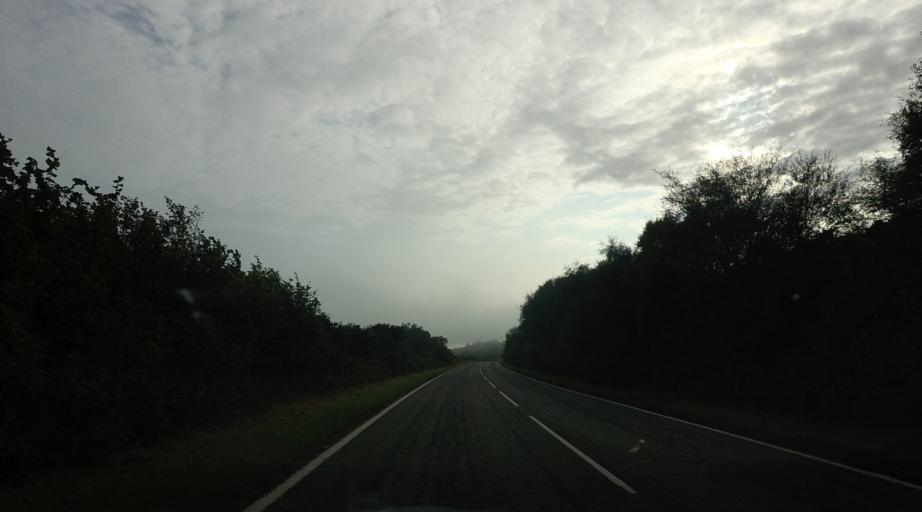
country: GB
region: Scotland
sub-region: Highland
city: Brora
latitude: 58.0556
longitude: -3.8101
